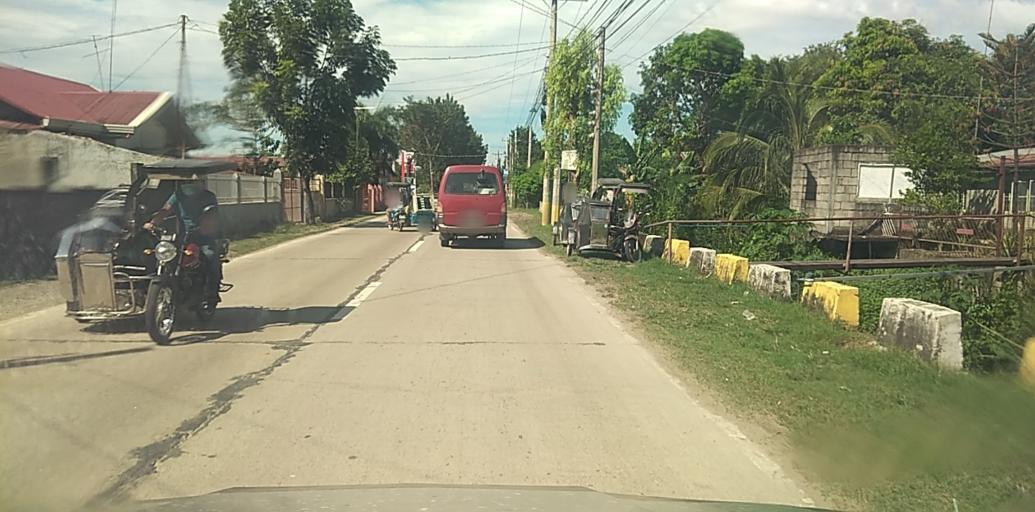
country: PH
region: Central Luzon
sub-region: Province of Pampanga
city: Arayat
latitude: 15.1505
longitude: 120.7468
